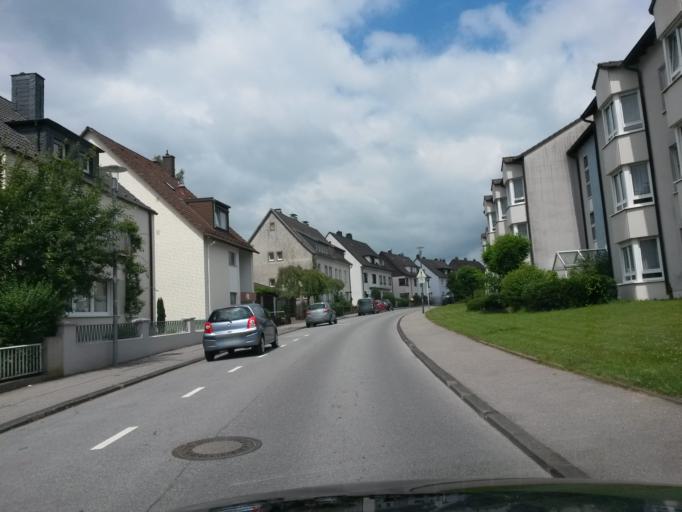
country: DE
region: North Rhine-Westphalia
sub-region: Regierungsbezirk Arnsberg
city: Luedenscheid
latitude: 51.2208
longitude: 7.6169
